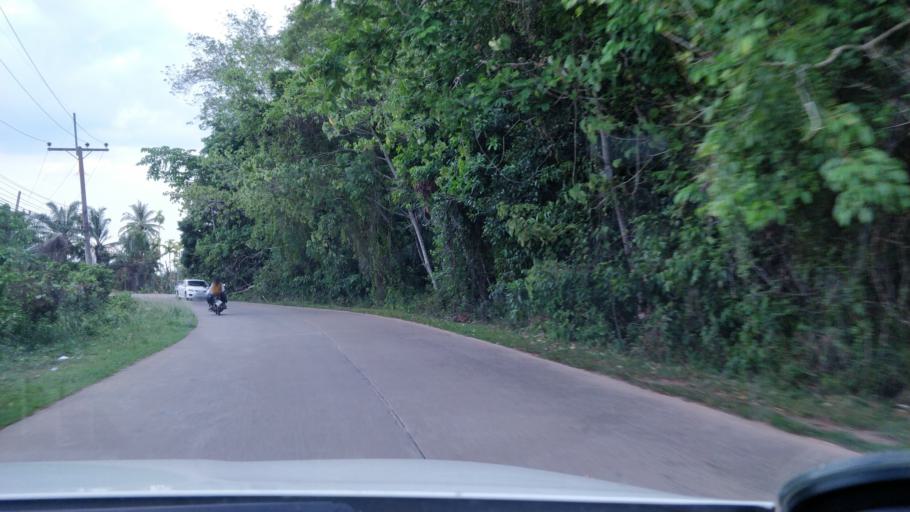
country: TH
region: Krabi
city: Saladan
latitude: 7.5788
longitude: 99.0679
